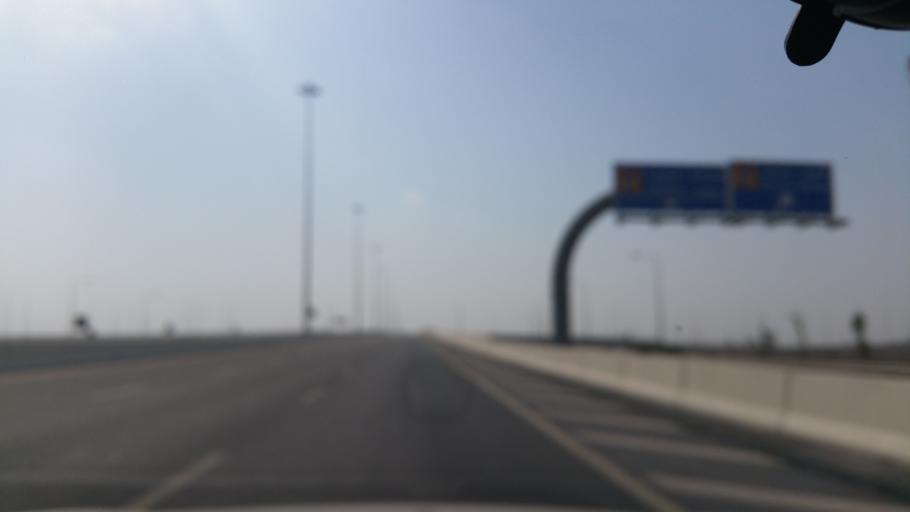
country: QA
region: Baladiyat Umm Salal
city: Umm Salal `Ali
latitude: 25.4570
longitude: 51.4838
